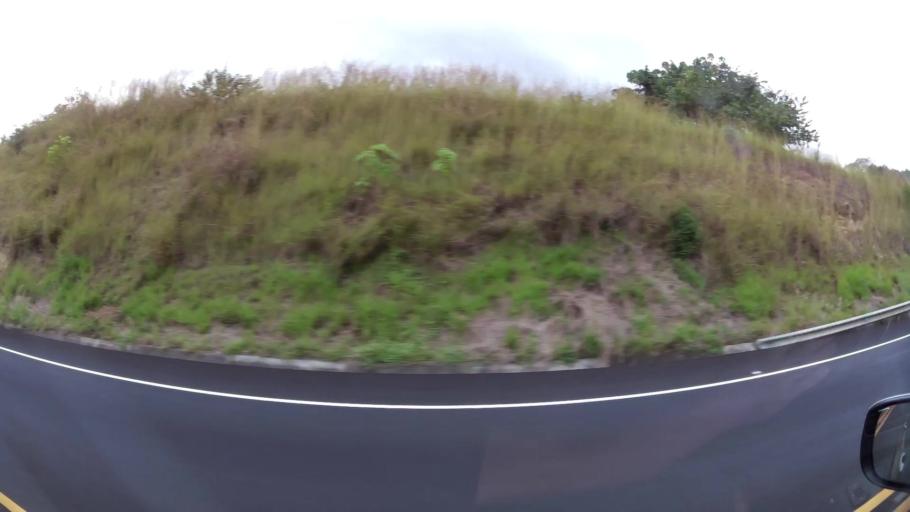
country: CR
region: Alajuela
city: Atenas
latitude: 9.9344
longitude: -84.4194
